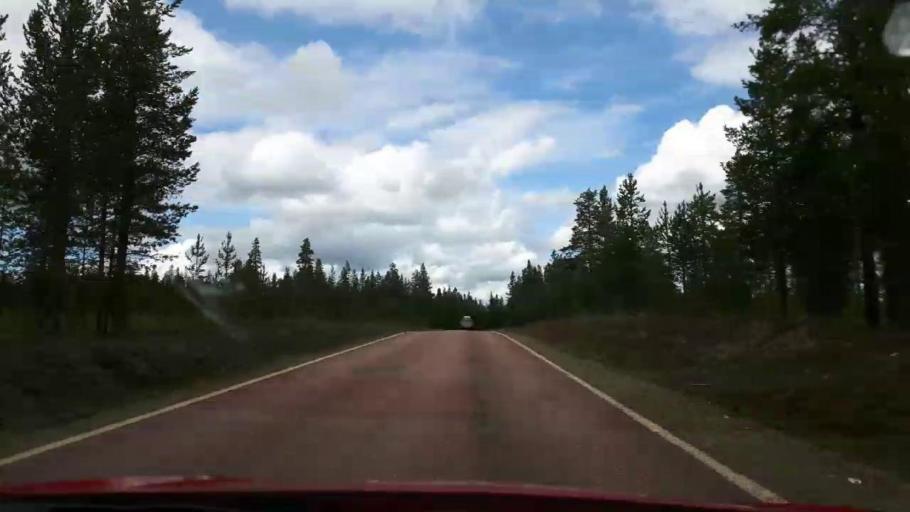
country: NO
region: Hedmark
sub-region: Trysil
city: Innbygda
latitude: 61.8554
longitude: 12.9483
